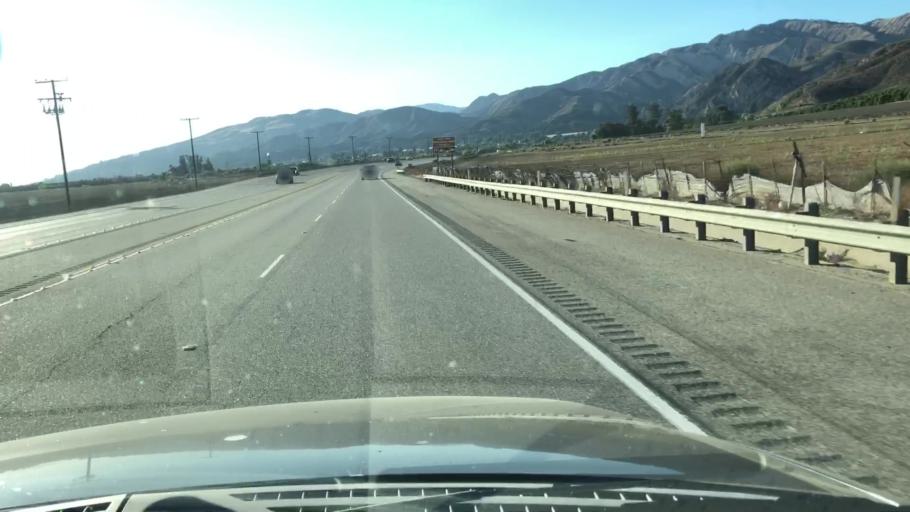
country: US
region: California
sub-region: Ventura County
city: Piru
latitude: 34.4083
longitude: -118.7741
